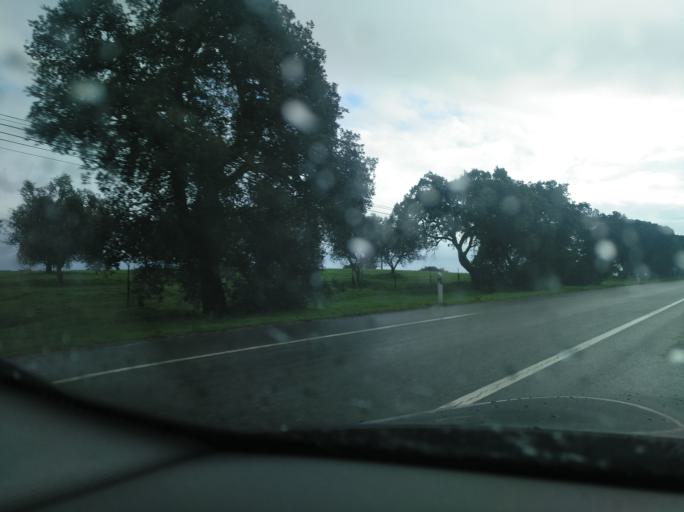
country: PT
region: Setubal
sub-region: Grandola
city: Grandola
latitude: 38.1003
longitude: -8.4184
